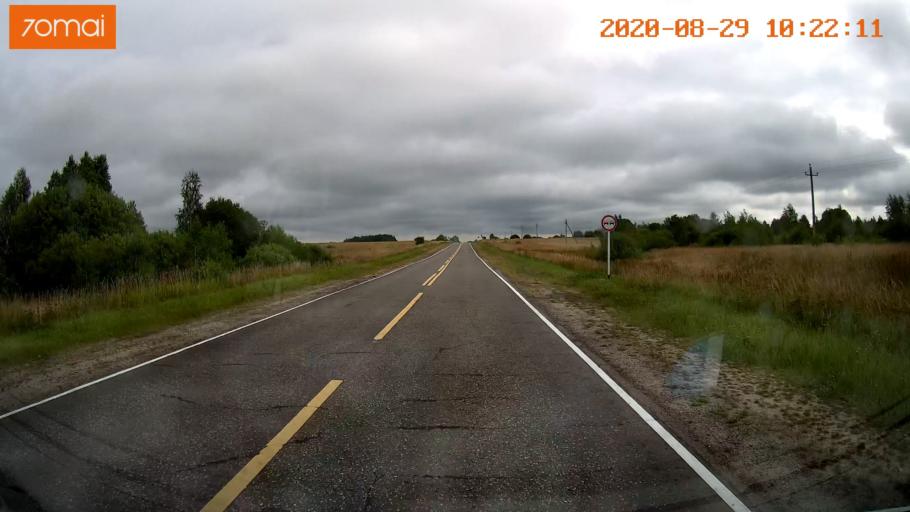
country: RU
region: Ivanovo
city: Yur'yevets
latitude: 57.3233
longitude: 42.9502
